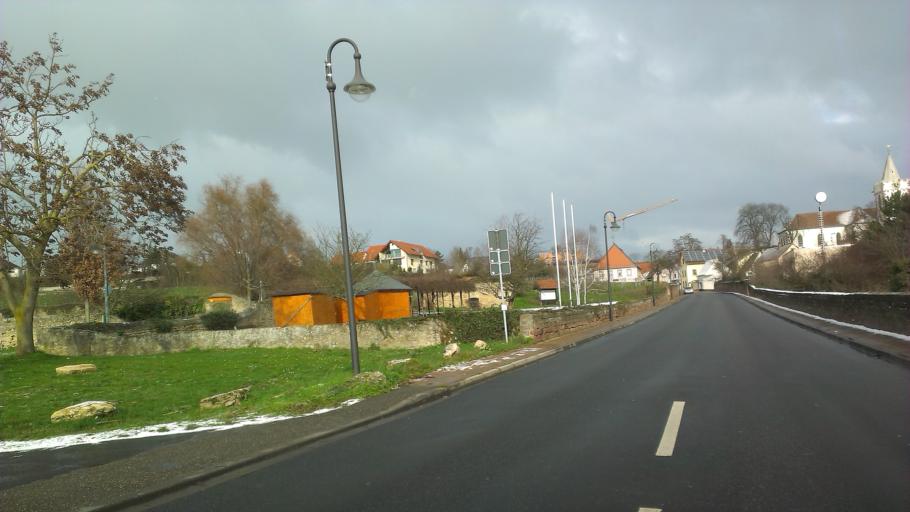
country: DE
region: Rheinland-Pfalz
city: Bockenheim
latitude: 49.6097
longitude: 8.1817
